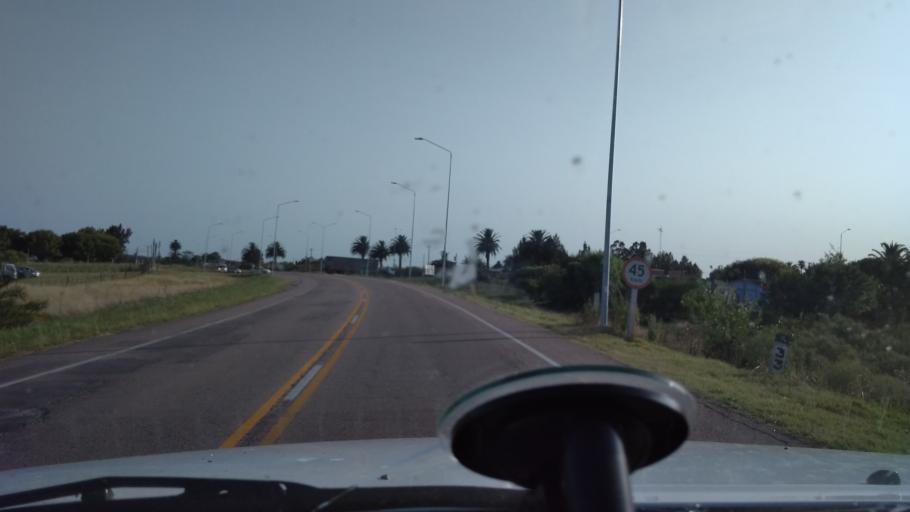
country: UY
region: Canelones
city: Sauce
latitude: -34.6629
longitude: -56.0575
